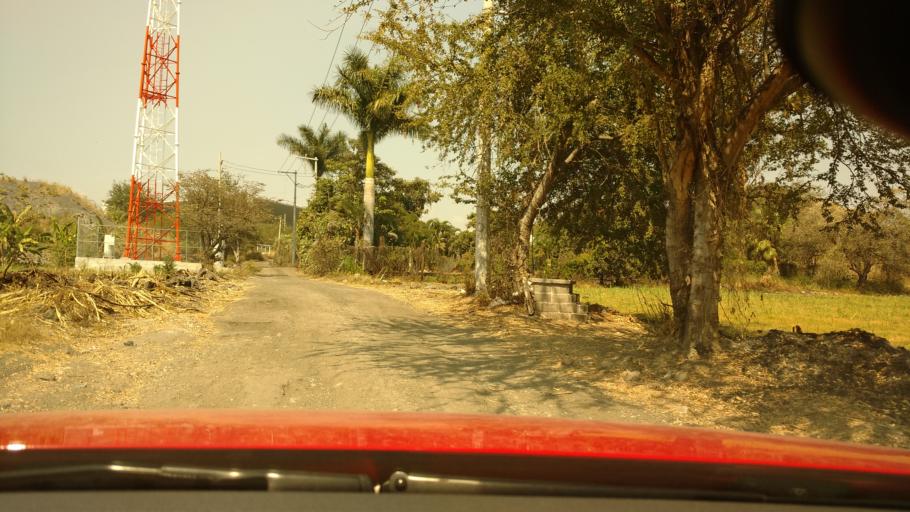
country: MX
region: Morelos
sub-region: Xochitepec
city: Chiconcuac
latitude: 18.8020
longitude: -99.2184
